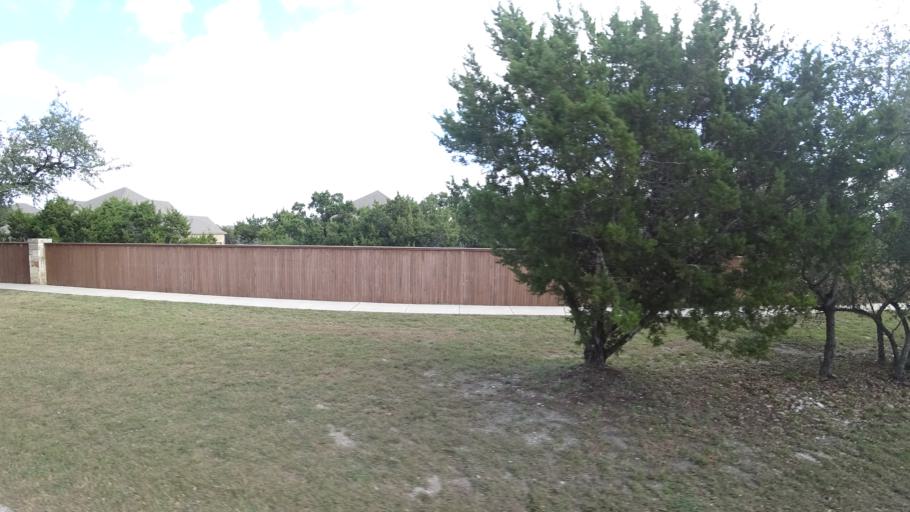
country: US
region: Texas
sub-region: Travis County
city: Bee Cave
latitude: 30.2499
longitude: -97.9315
